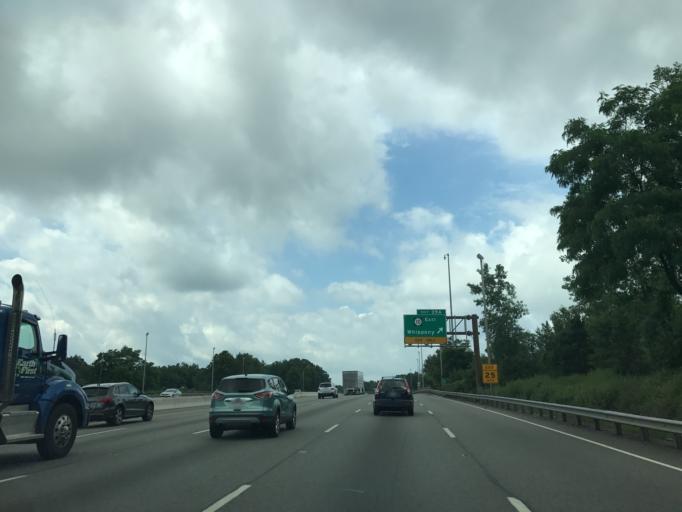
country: US
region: New Jersey
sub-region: Morris County
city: Parsippany
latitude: 40.8340
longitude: -74.4375
